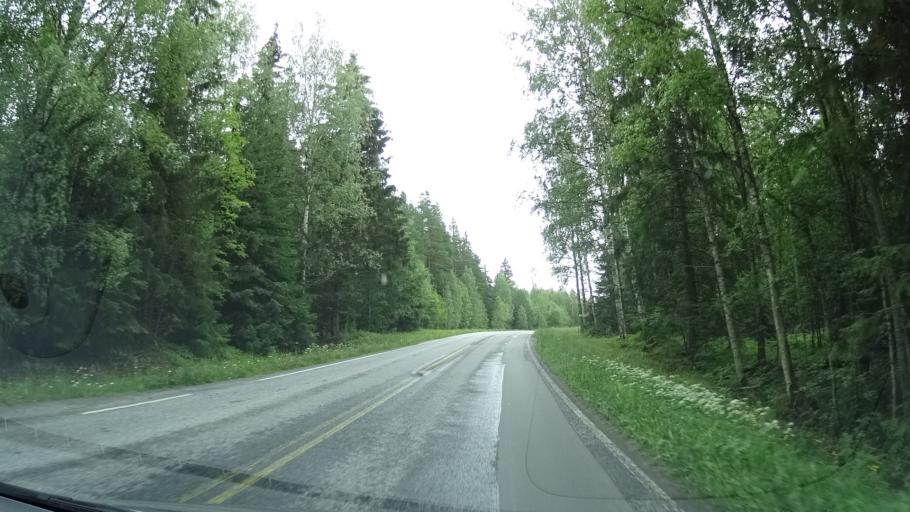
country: FI
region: Pirkanmaa
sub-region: Etelae-Pirkanmaa
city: Urjala
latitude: 61.0869
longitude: 23.5184
